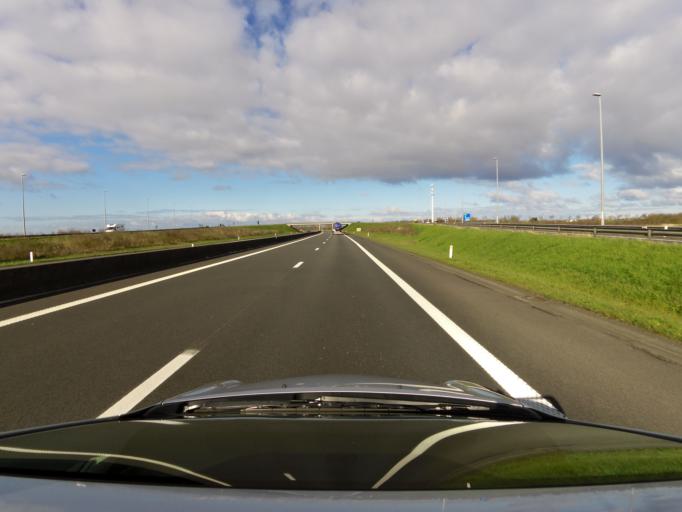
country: BE
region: Flanders
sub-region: Provincie West-Vlaanderen
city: De Panne
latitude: 51.0686
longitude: 2.6080
